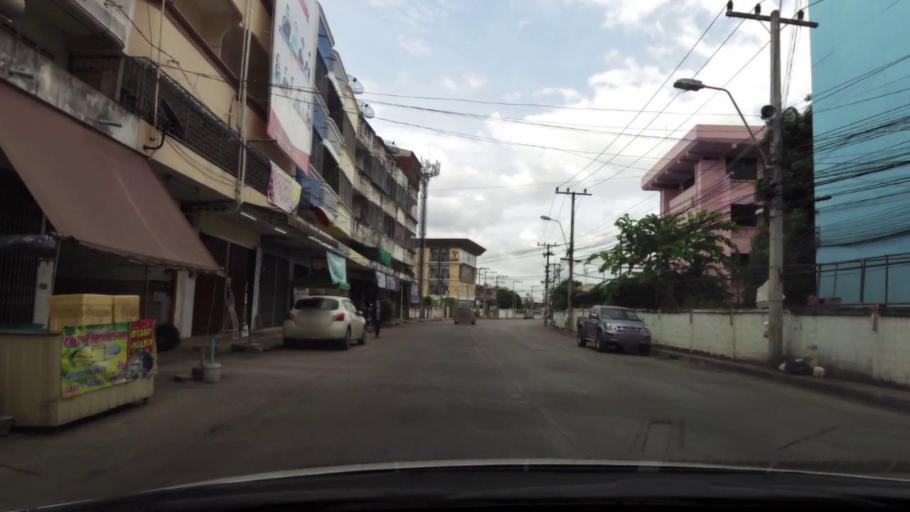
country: TH
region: Ratchaburi
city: Ratchaburi
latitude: 13.5366
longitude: 99.8282
